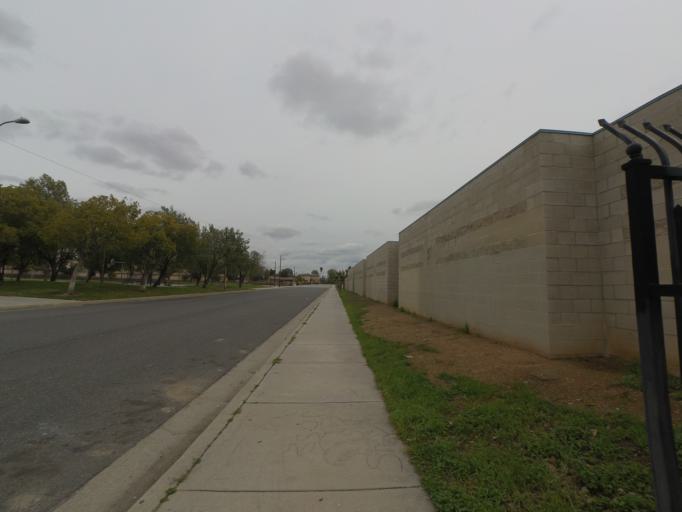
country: US
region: California
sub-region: Riverside County
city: March Air Force Base
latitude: 33.9183
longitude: -117.2680
